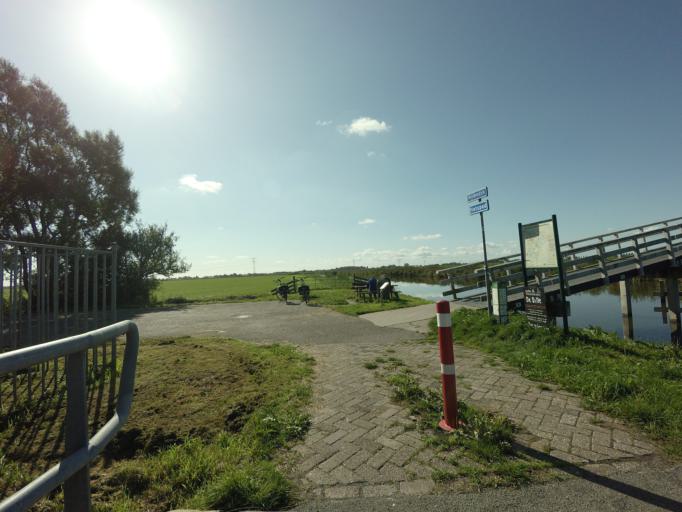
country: NL
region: Friesland
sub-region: Gemeente Boarnsterhim
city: Reduzum
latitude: 53.1204
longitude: 5.7564
